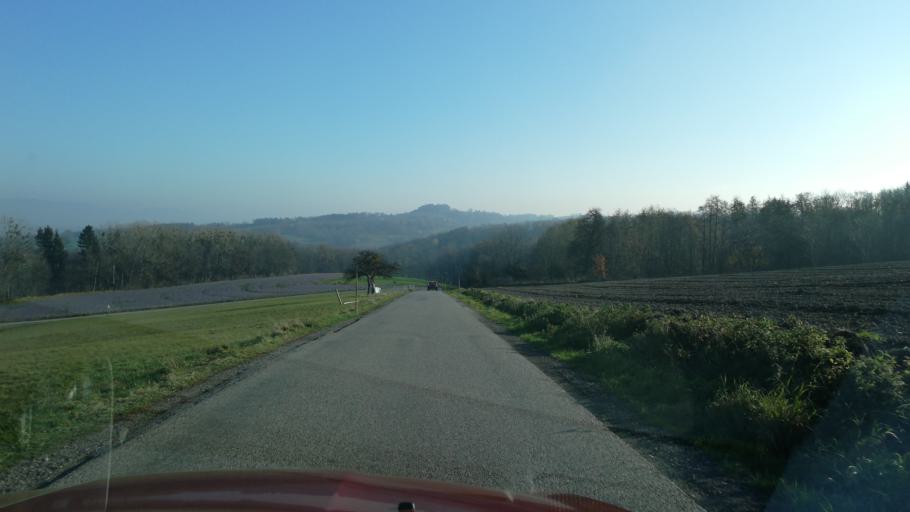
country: AT
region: Upper Austria
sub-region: Wels-Land
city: Buchkirchen
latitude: 48.2606
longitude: 14.0117
